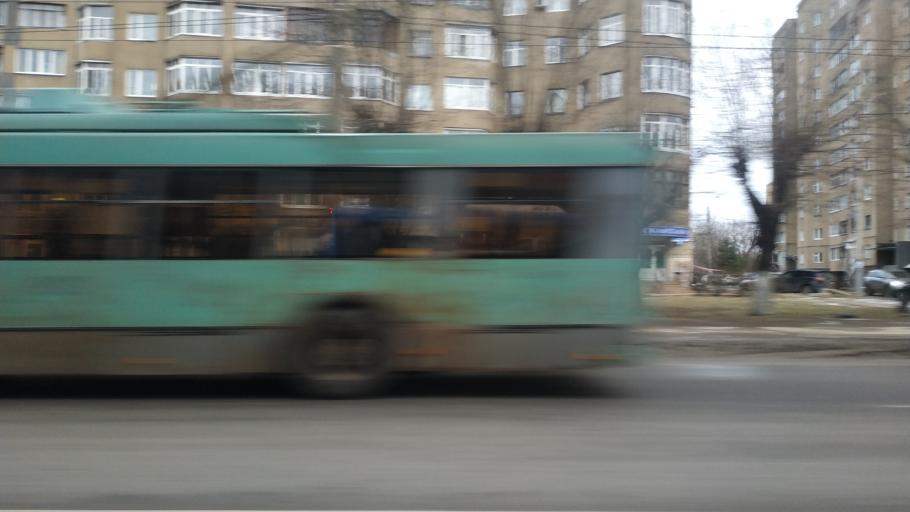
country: RU
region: Tverskaya
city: Tver
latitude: 56.8525
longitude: 35.9259
